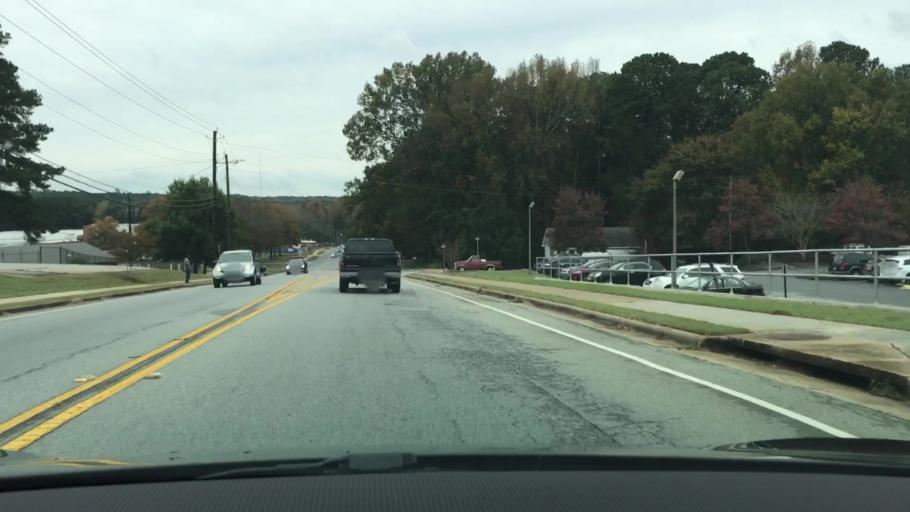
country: US
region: Georgia
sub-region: Greene County
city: Greensboro
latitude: 33.5667
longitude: -83.1837
